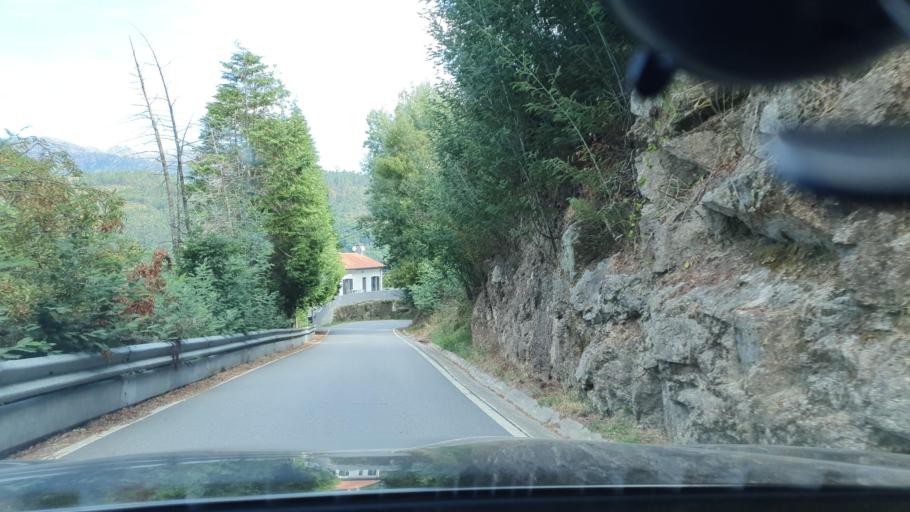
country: PT
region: Braga
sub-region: Vieira do Minho
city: Vieira do Minho
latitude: 41.6879
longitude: -8.0910
